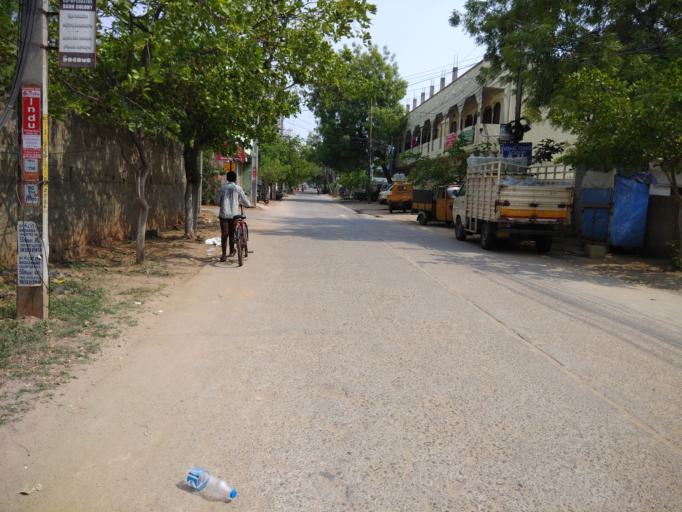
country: IN
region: Telangana
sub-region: Rangareddi
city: Lal Bahadur Nagar
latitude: 17.3717
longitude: 78.5612
